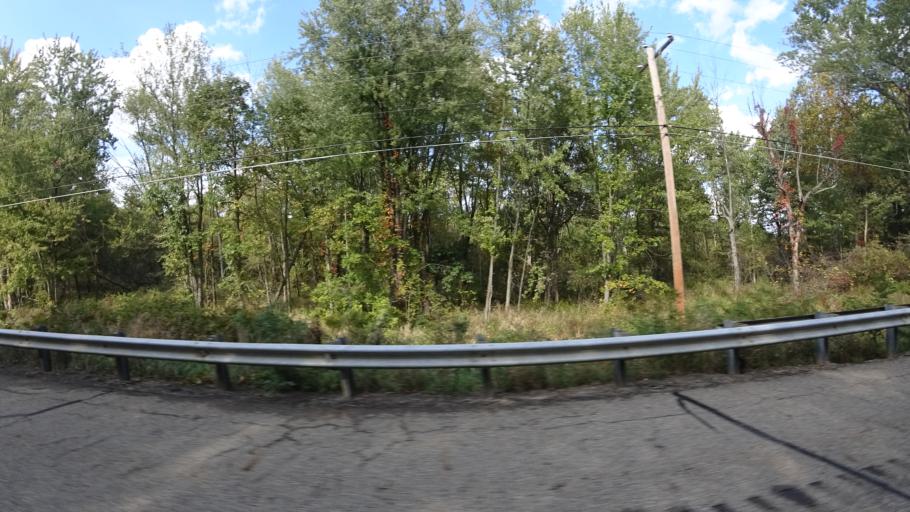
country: US
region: Michigan
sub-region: Branch County
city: Union City
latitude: 42.1047
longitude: -85.0362
